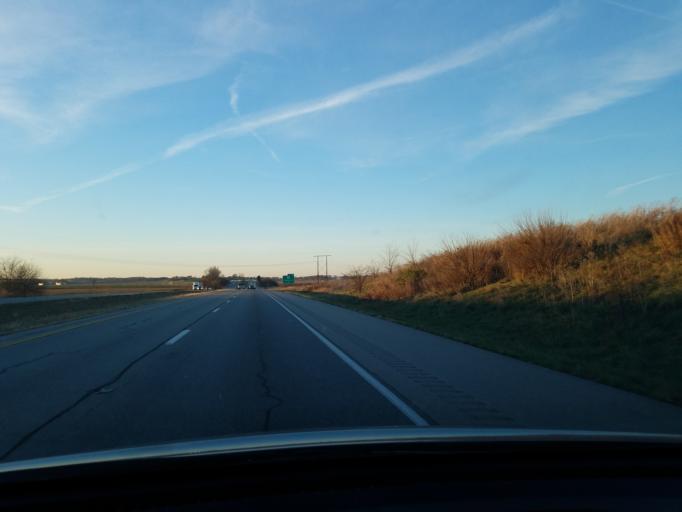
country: US
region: Indiana
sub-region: Posey County
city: Poseyville
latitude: 38.1752
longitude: -87.7569
